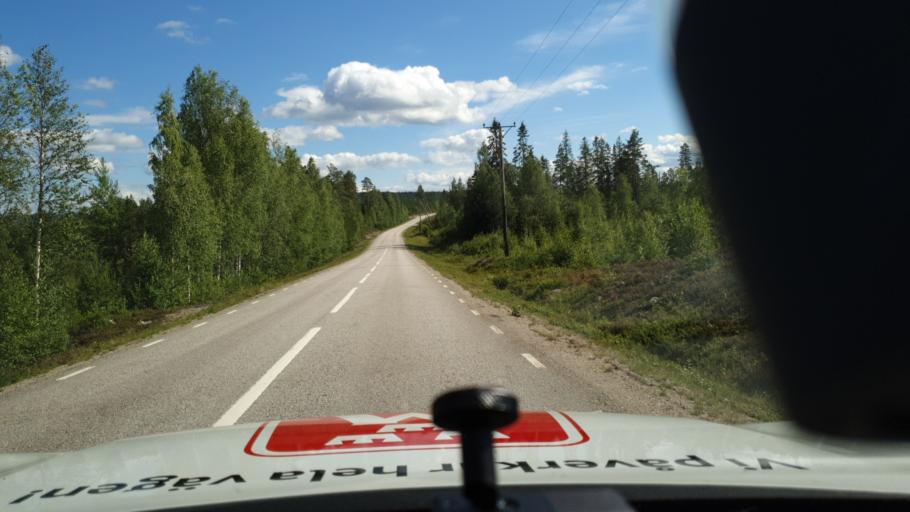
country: NO
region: Hedmark
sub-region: Trysil
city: Innbygda
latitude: 60.9962
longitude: 12.4899
